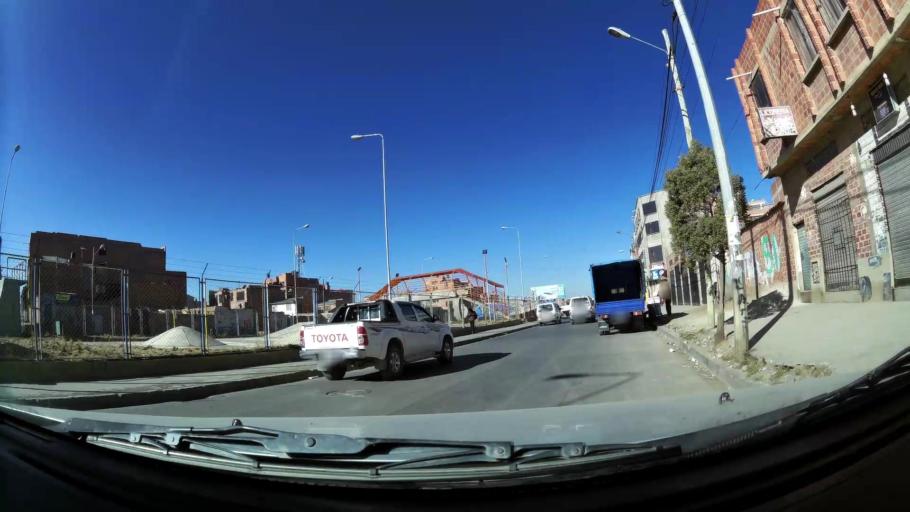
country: BO
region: La Paz
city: La Paz
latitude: -16.5287
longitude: -68.1601
